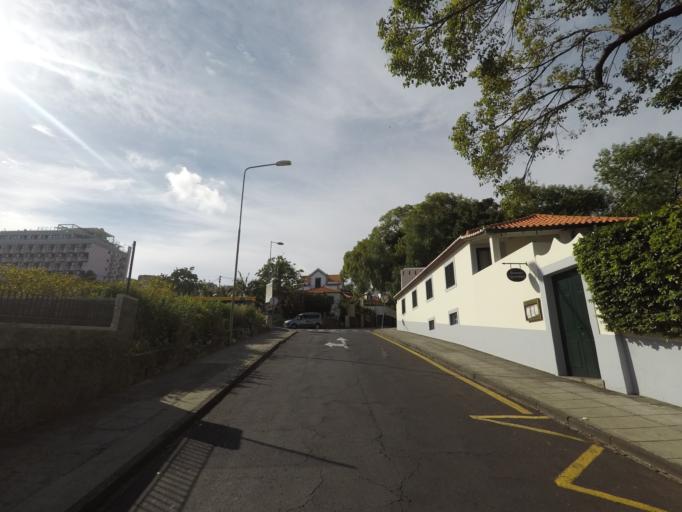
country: PT
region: Madeira
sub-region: Funchal
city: Funchal
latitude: 32.6413
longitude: -16.9274
